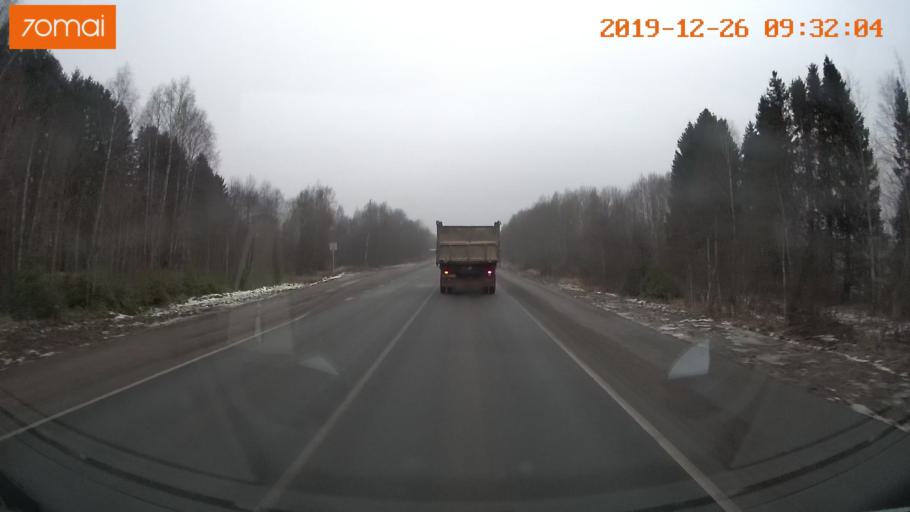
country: RU
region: Vologda
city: Gryazovets
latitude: 59.0745
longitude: 40.1209
